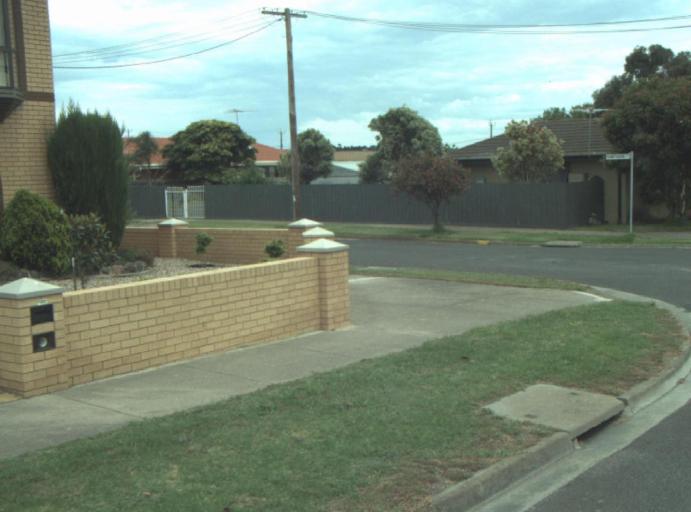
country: AU
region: Victoria
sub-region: Greater Geelong
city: Clifton Springs
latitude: -38.1206
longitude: 144.6292
